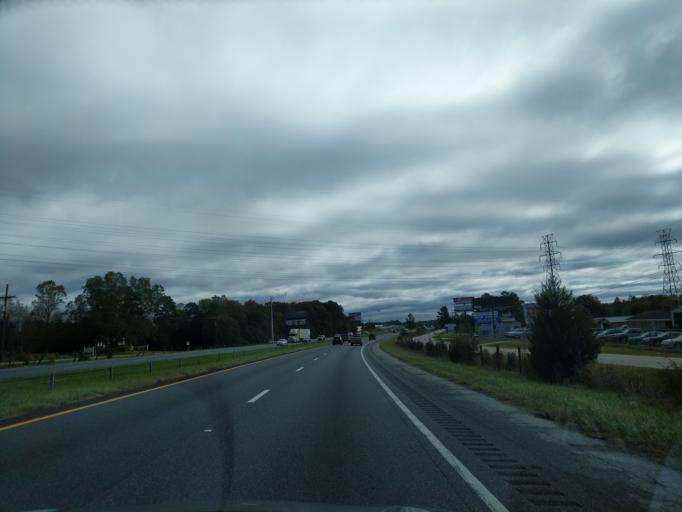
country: US
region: South Carolina
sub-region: Cherokee County
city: East Gaffney
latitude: 35.1012
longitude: -81.6447
